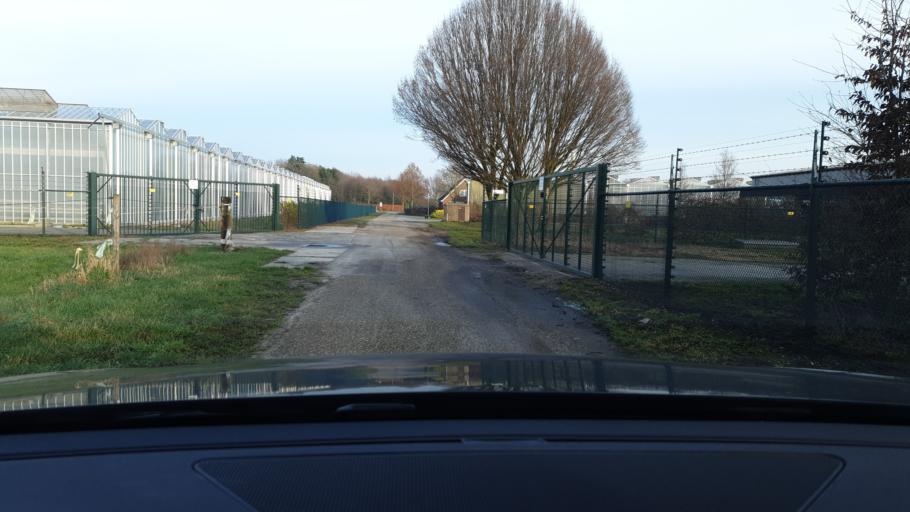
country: NL
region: Limburg
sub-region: Gemeente Venray
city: Venray
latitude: 51.4680
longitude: 6.0412
